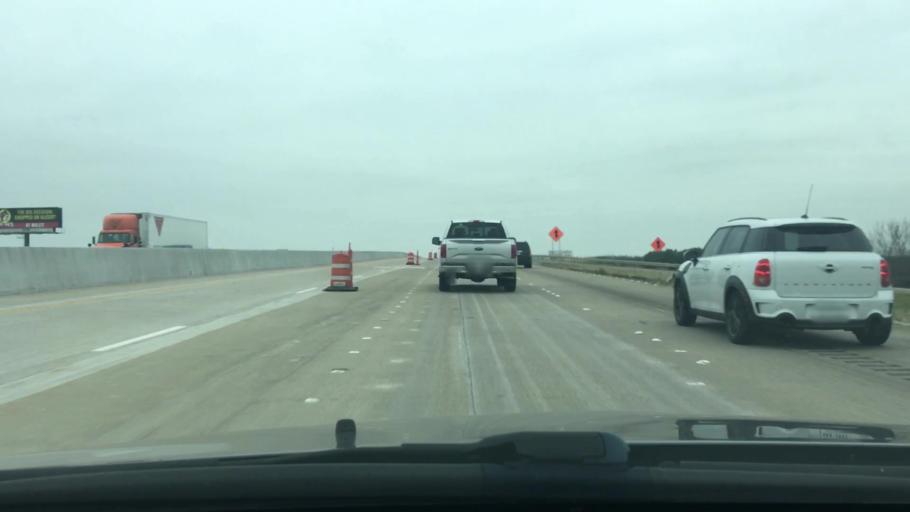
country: US
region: Texas
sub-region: Navarro County
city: Corsicana
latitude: 32.0971
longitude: -96.4410
